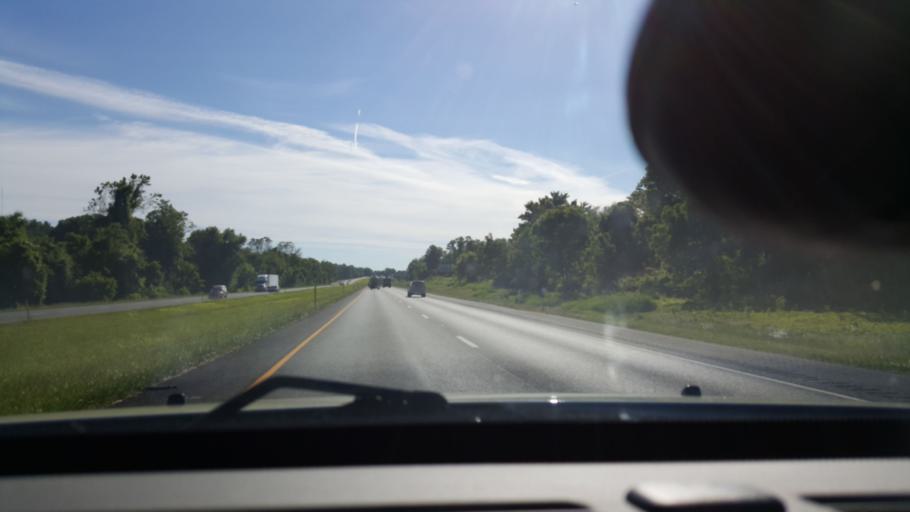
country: US
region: Pennsylvania
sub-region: York County
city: Yorklyn
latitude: 40.0021
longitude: -76.6293
